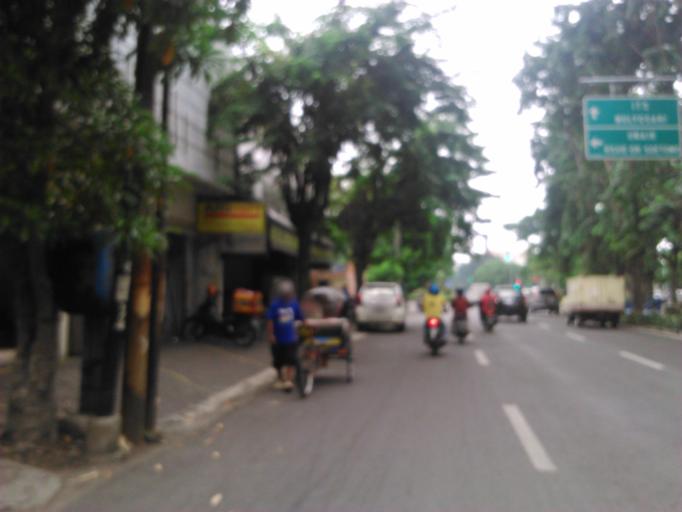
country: ID
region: East Java
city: Gubengairlangga
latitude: -7.2790
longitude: 112.7611
